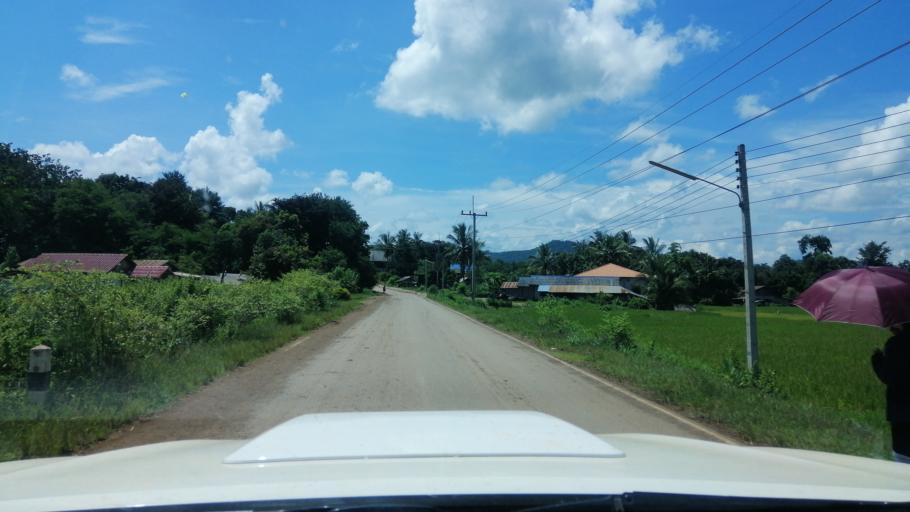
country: TH
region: Uttaradit
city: Ban Khok
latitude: 18.1358
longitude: 101.2732
